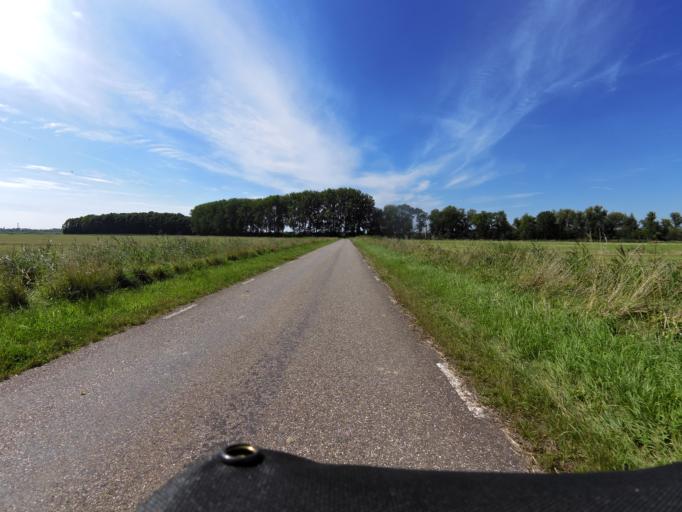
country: NL
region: South Holland
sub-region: Gemeente Sliedrecht
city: Sliedrecht
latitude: 51.7736
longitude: 4.8131
